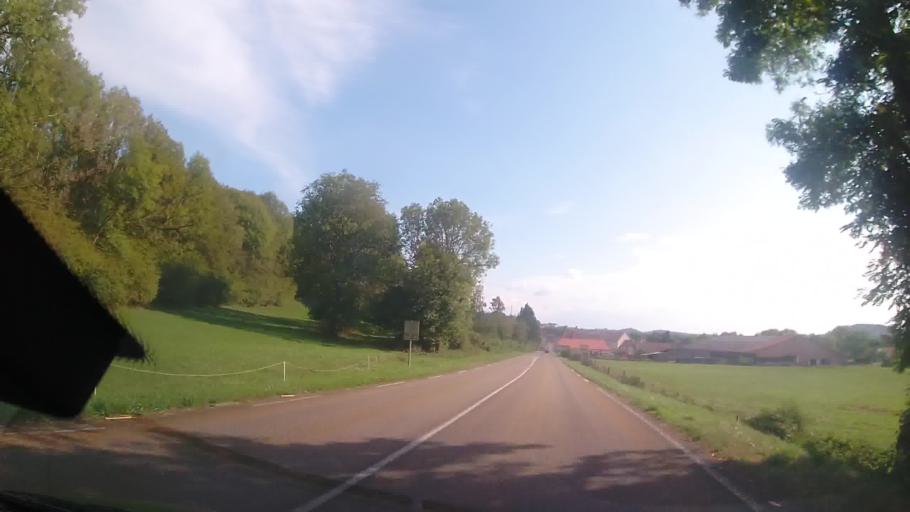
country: FR
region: Franche-Comte
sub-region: Departement du Jura
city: Clairvaux-les-Lacs
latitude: 46.5856
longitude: 5.7593
